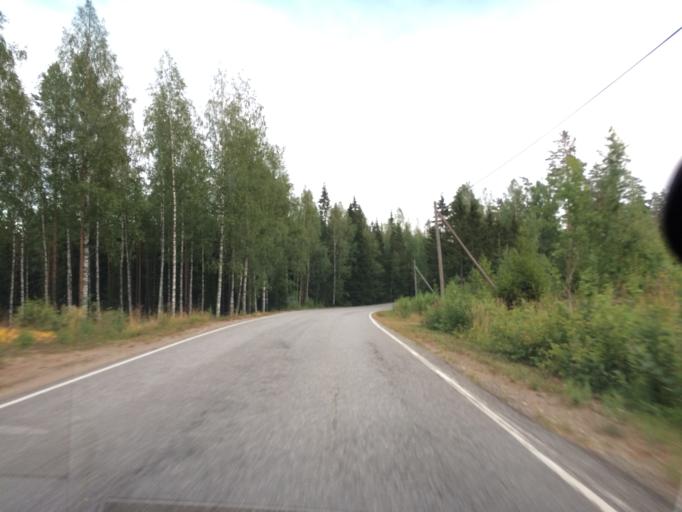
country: FI
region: Haeme
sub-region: Haemeenlinna
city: Tuulos
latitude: 61.2270
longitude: 24.7114
